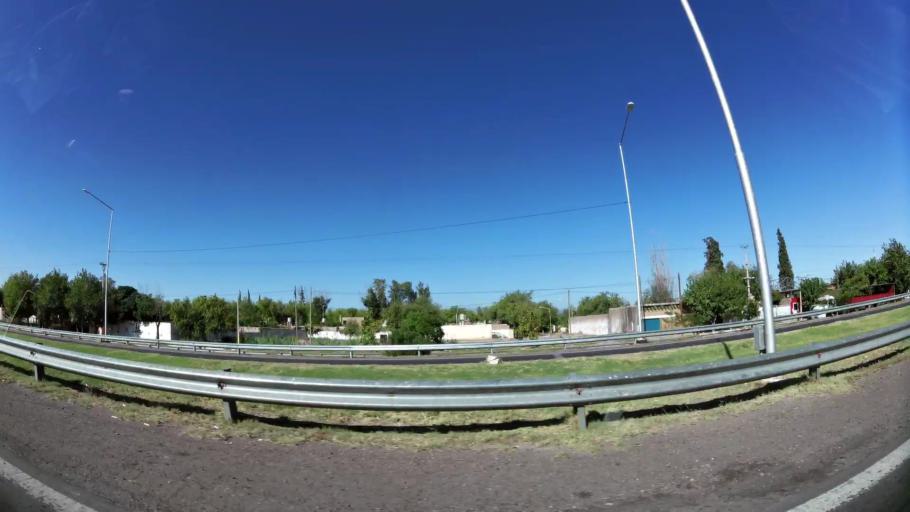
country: AR
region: San Juan
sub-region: Departamento de Santa Lucia
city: Santa Lucia
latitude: -31.5235
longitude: -68.5030
